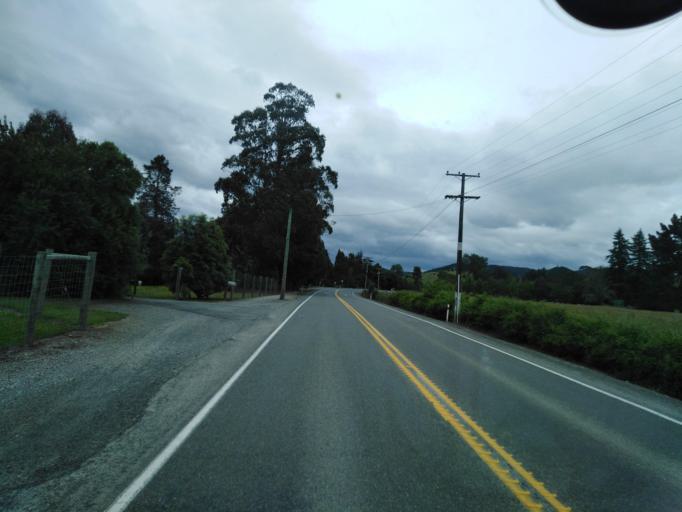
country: NZ
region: Tasman
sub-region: Tasman District
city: Wakefield
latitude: -41.4527
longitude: 172.9573
